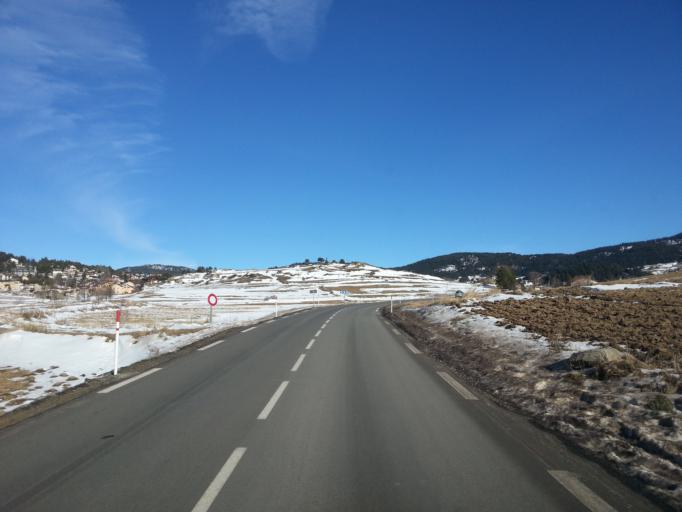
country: ES
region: Catalonia
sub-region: Provincia de Girona
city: Llivia
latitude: 42.5200
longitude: 2.1174
